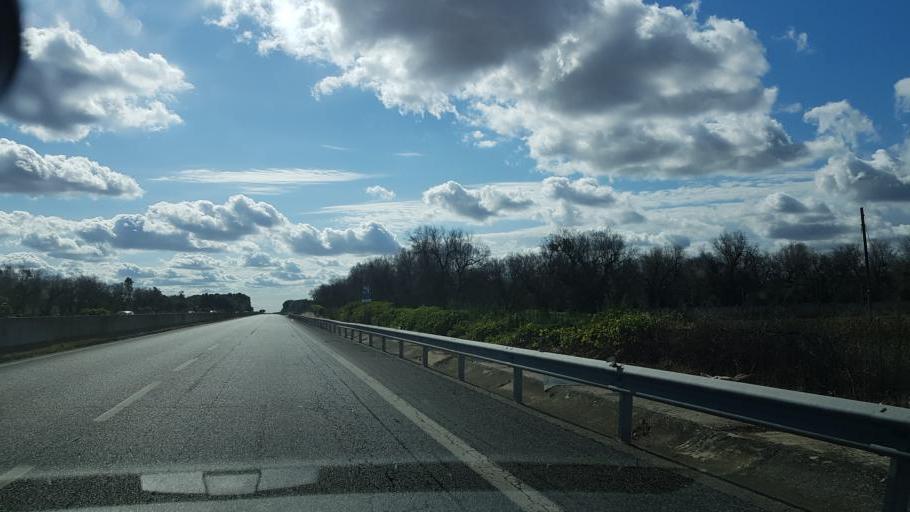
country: IT
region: Apulia
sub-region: Provincia di Brindisi
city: Torchiarolo
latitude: 40.4828
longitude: 18.0430
